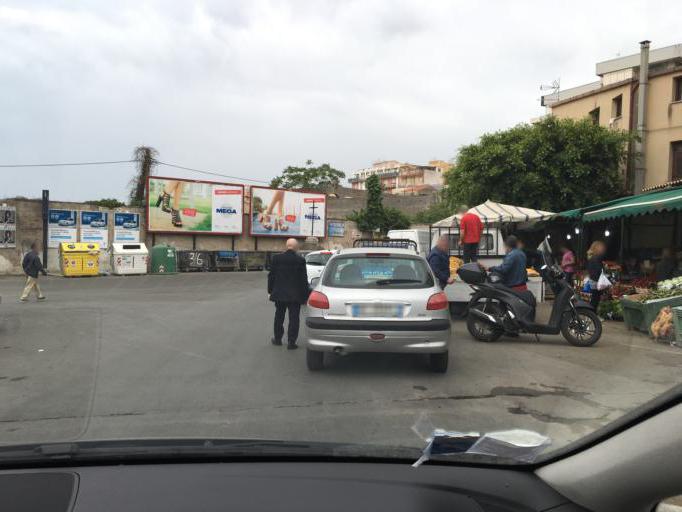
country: IT
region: Sicily
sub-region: Palermo
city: Palermo
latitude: 38.1115
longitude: 13.3392
